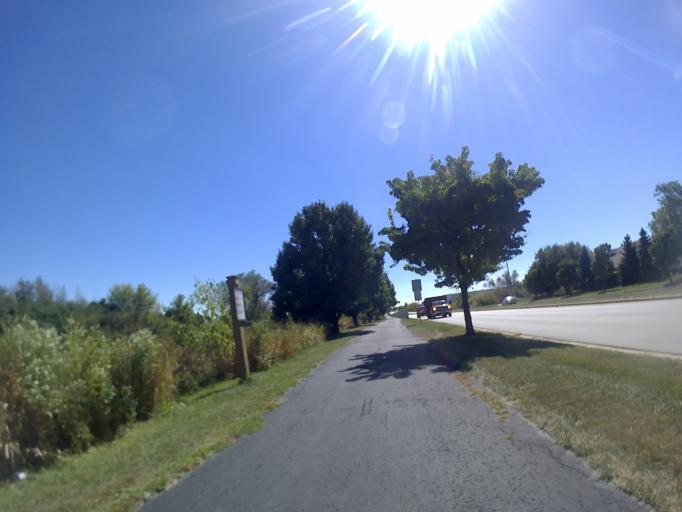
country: US
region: Illinois
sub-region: DuPage County
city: Woodridge
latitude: 41.7214
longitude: -88.0271
